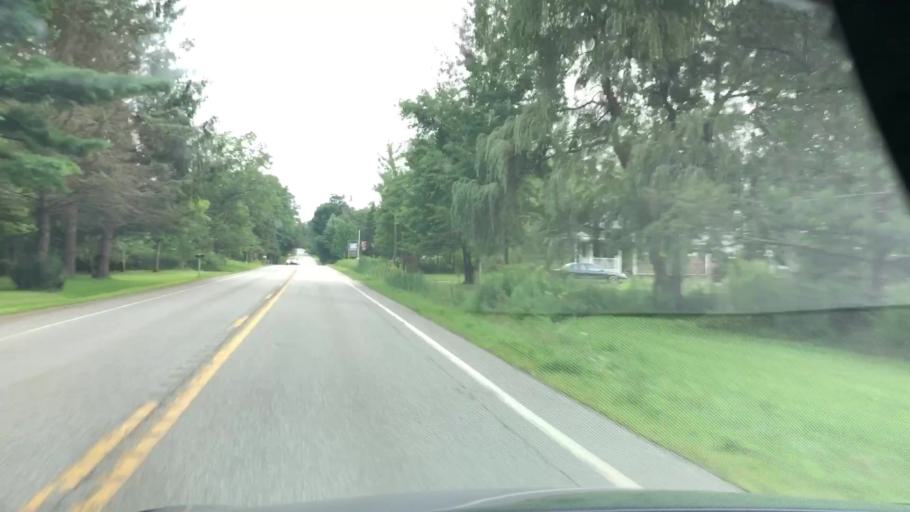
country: US
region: Pennsylvania
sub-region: Erie County
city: Union City
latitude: 41.9260
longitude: -79.8435
